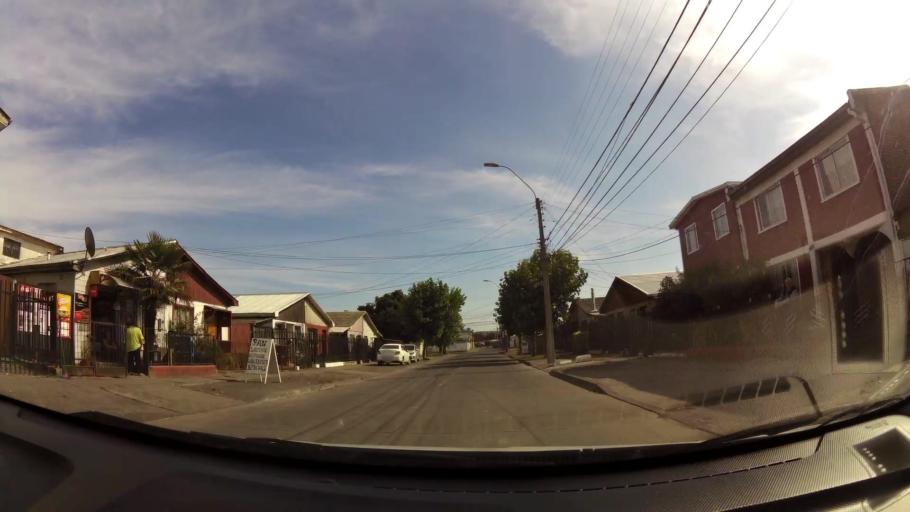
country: CL
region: Biobio
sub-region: Provincia de Concepcion
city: Talcahuano
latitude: -36.7853
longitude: -73.1065
